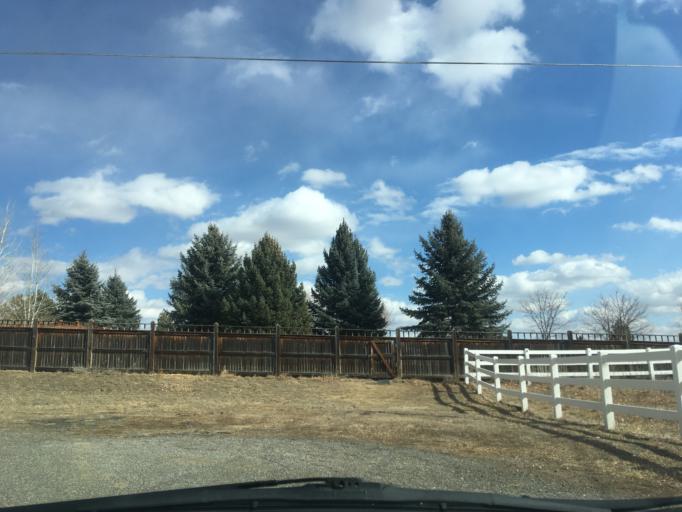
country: US
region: Colorado
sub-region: Boulder County
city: Lafayette
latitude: 39.9599
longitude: -105.0532
